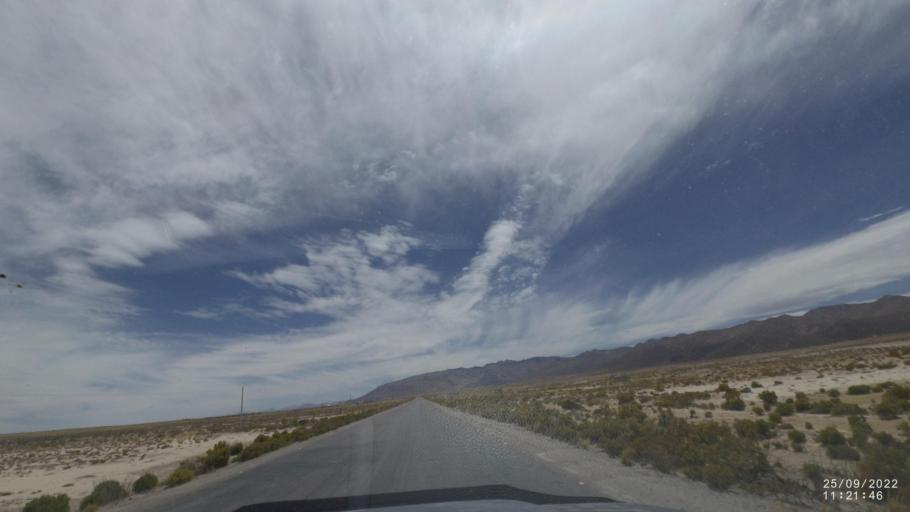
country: BO
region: Oruro
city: Challapata
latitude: -19.1378
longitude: -66.7697
